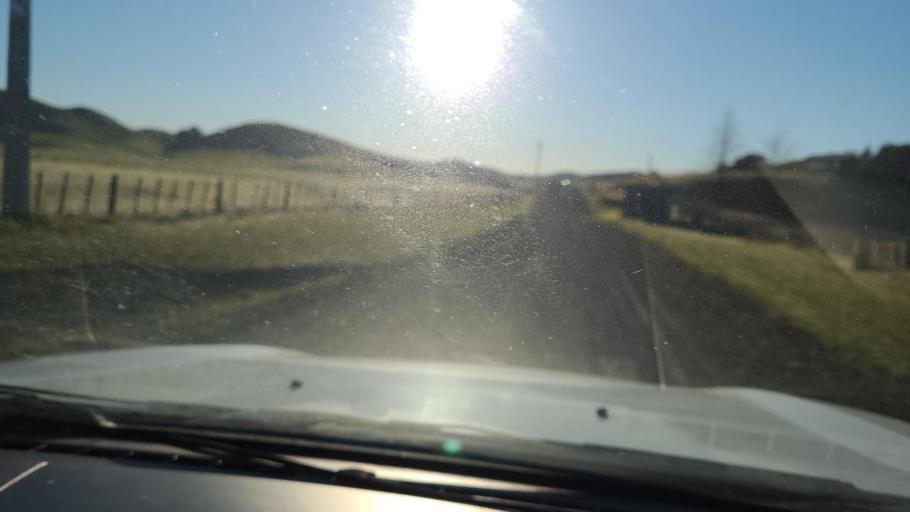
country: NZ
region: Hawke's Bay
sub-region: Hastings District
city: Hastings
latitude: -39.5893
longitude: 176.6584
